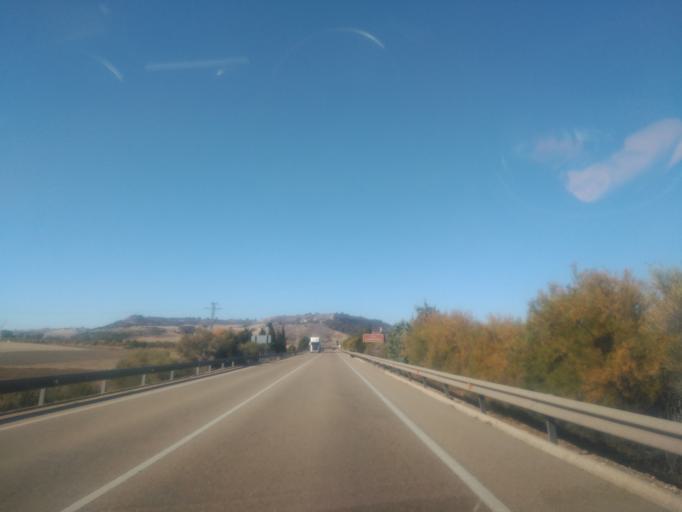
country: ES
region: Castille and Leon
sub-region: Provincia de Valladolid
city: Quintanilla de Arriba
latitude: 41.6176
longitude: -4.2137
